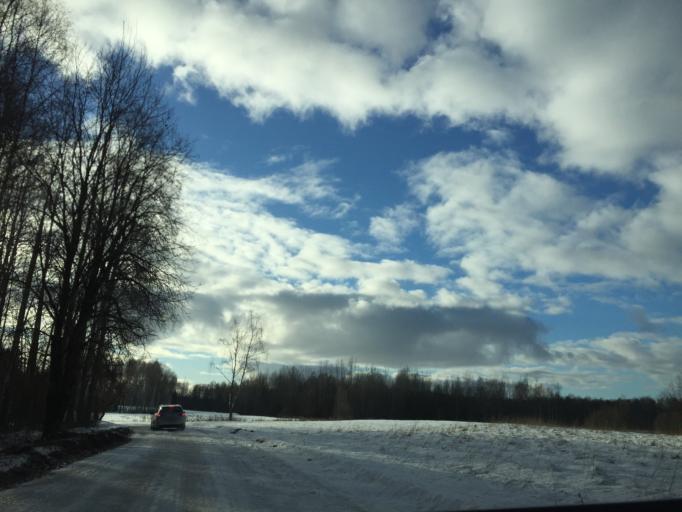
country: LV
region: Lielvarde
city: Lielvarde
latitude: 56.5715
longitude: 24.7989
